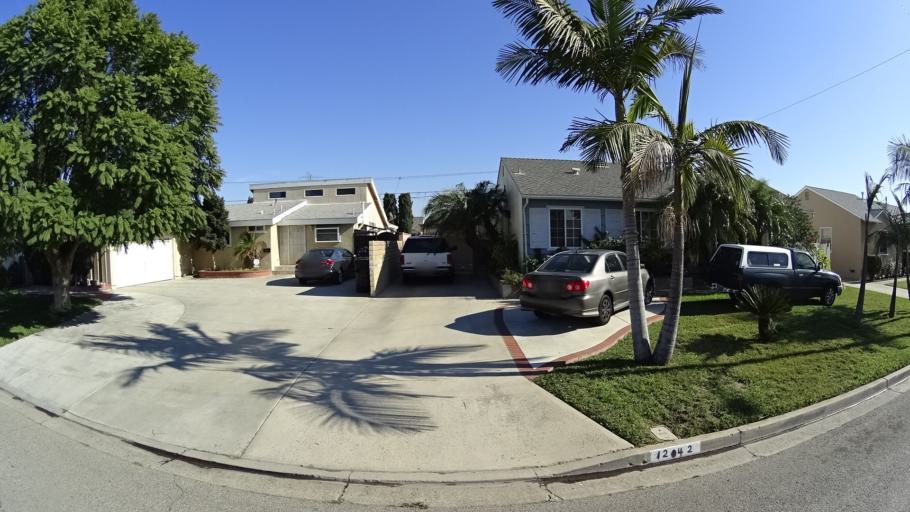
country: US
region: California
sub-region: Orange County
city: Garden Grove
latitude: 33.7881
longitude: -117.9304
